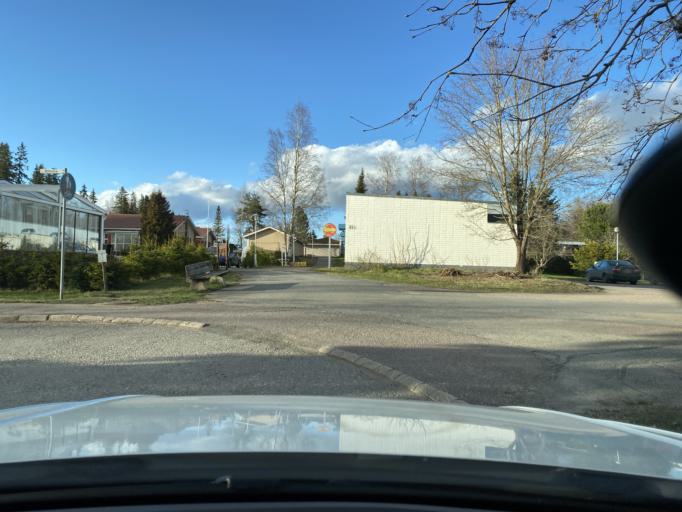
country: FI
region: Pirkanmaa
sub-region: Lounais-Pirkanmaa
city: Punkalaidun
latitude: 61.1140
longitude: 23.1030
